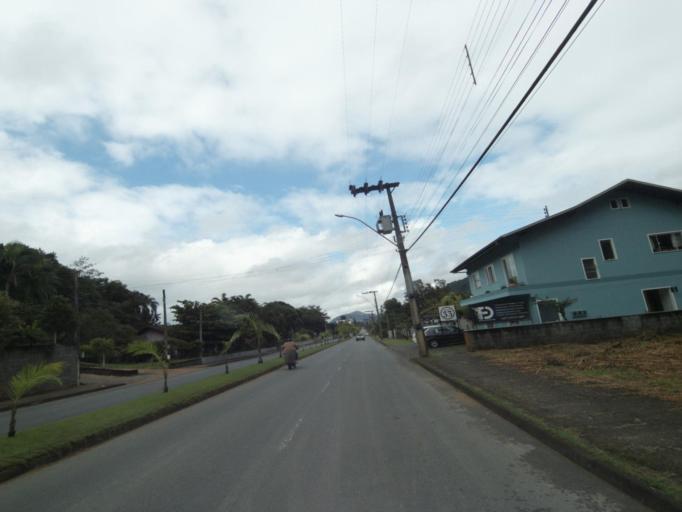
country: BR
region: Santa Catarina
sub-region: Pomerode
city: Pomerode
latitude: -26.7254
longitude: -49.1796
